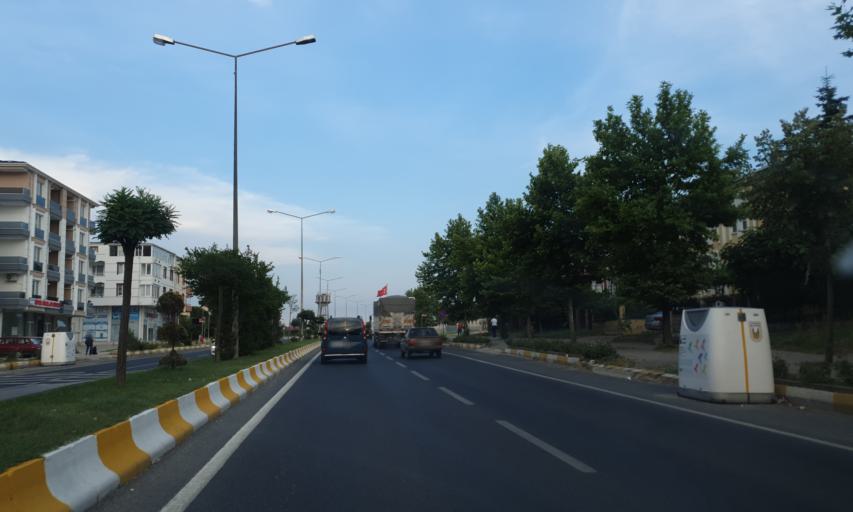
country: TR
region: Kirklareli
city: Luleburgaz
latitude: 41.4005
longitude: 27.3725
